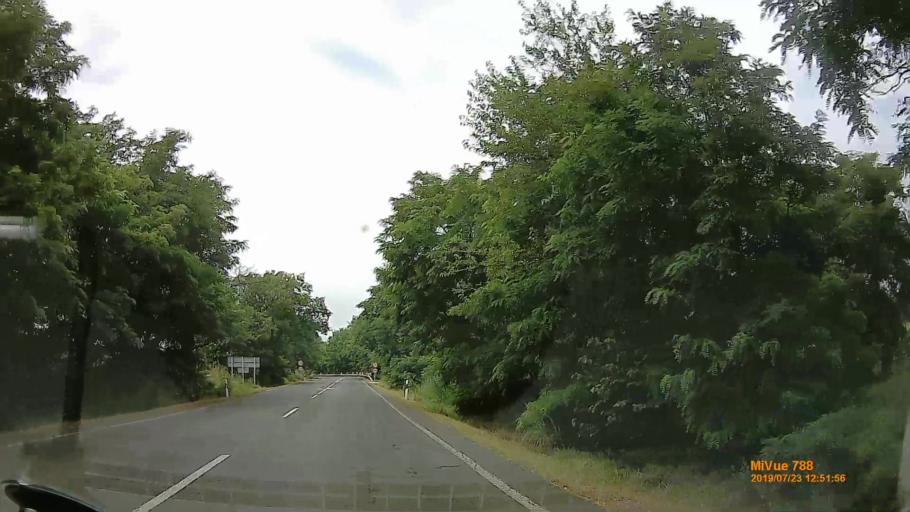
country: HU
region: Szabolcs-Szatmar-Bereg
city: Nagycserkesz
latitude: 47.9611
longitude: 21.5753
